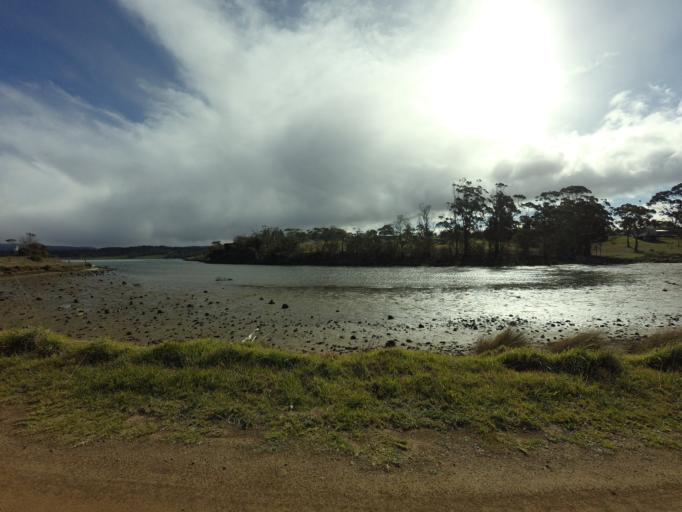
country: AU
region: Tasmania
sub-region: Sorell
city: Sorell
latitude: -42.3095
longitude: 147.9963
